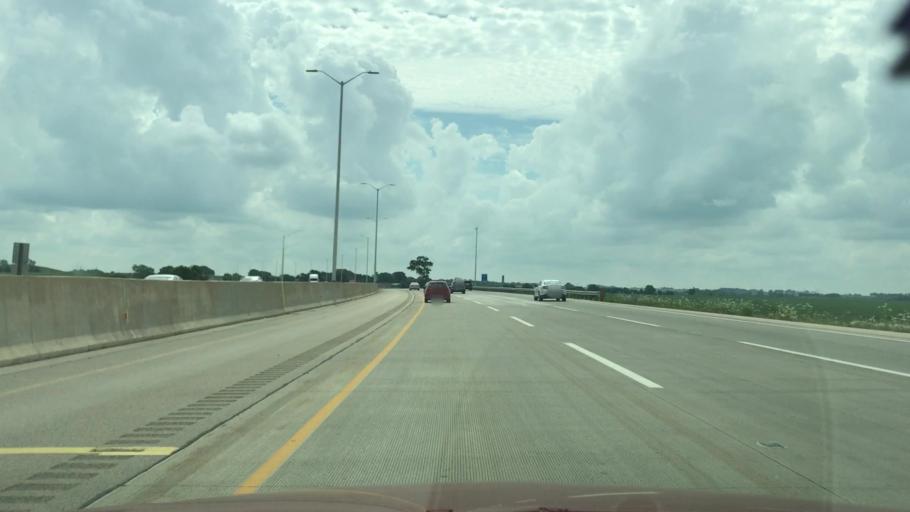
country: US
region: Illinois
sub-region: Winnebago County
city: Cherry Valley
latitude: 42.2361
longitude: -88.9123
